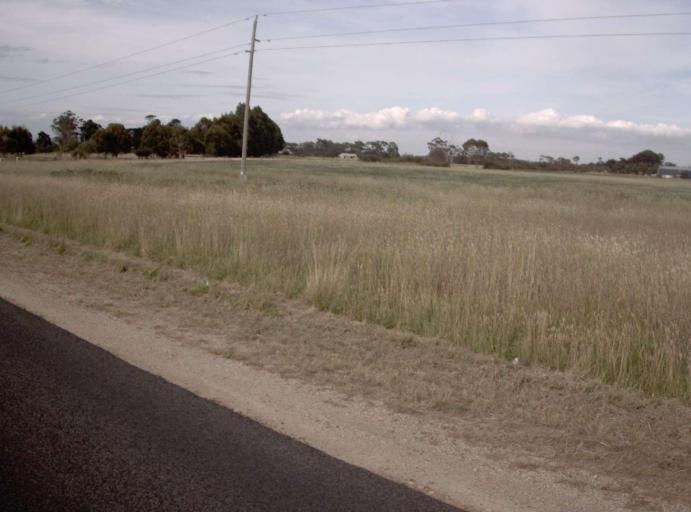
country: AU
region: Victoria
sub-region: Wellington
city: Heyfield
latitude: -38.0060
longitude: 146.7803
